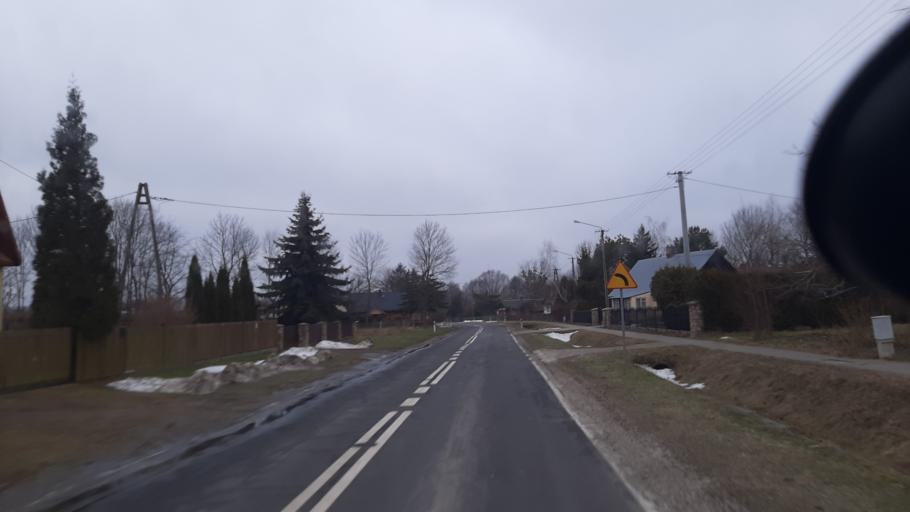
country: PL
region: Lublin Voivodeship
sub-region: Powiat wlodawski
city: Hansk
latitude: 51.5626
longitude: 23.3829
